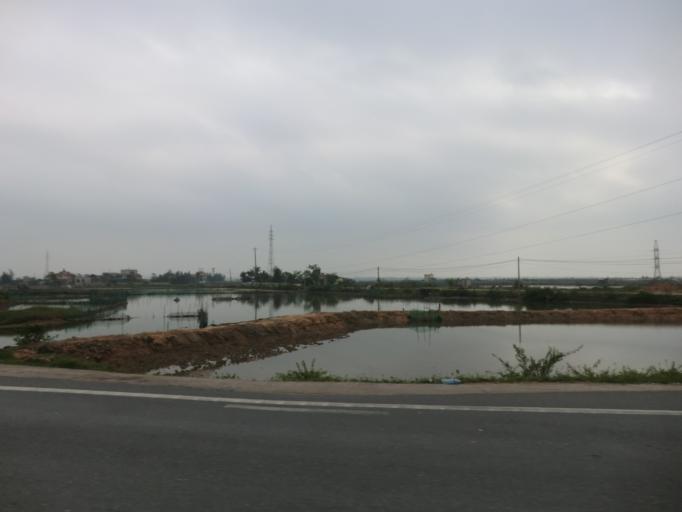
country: VN
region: Quang Binh
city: Ba Don
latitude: 17.7045
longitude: 106.4408
